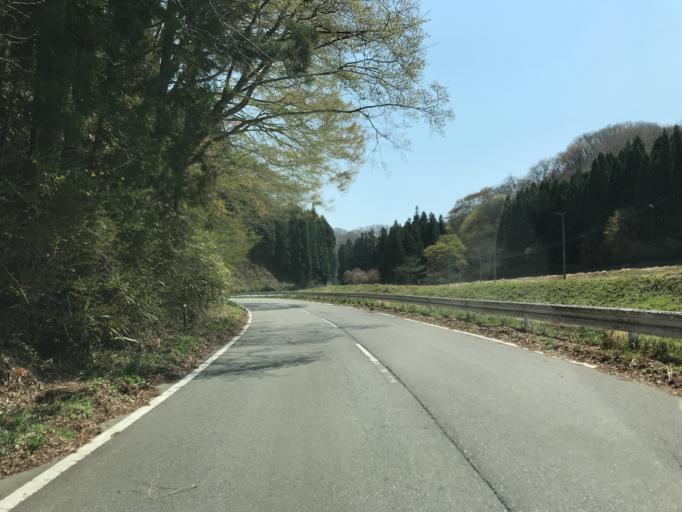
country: JP
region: Fukushima
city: Ishikawa
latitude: 36.9865
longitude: 140.6178
